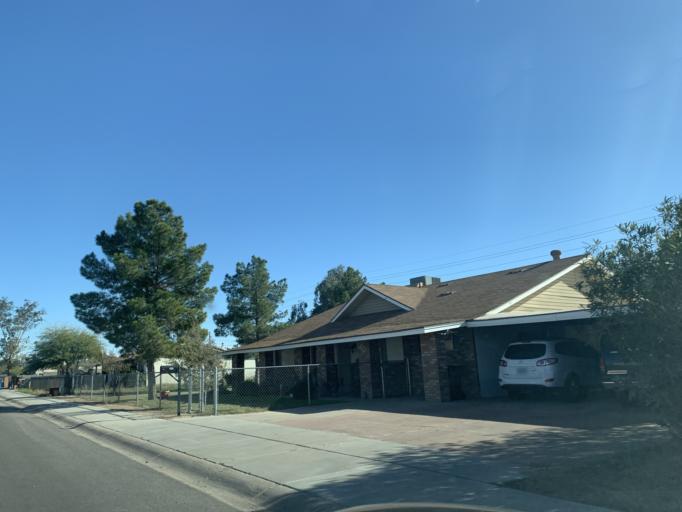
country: US
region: Arizona
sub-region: Maricopa County
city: Laveen
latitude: 33.3928
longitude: -112.1439
